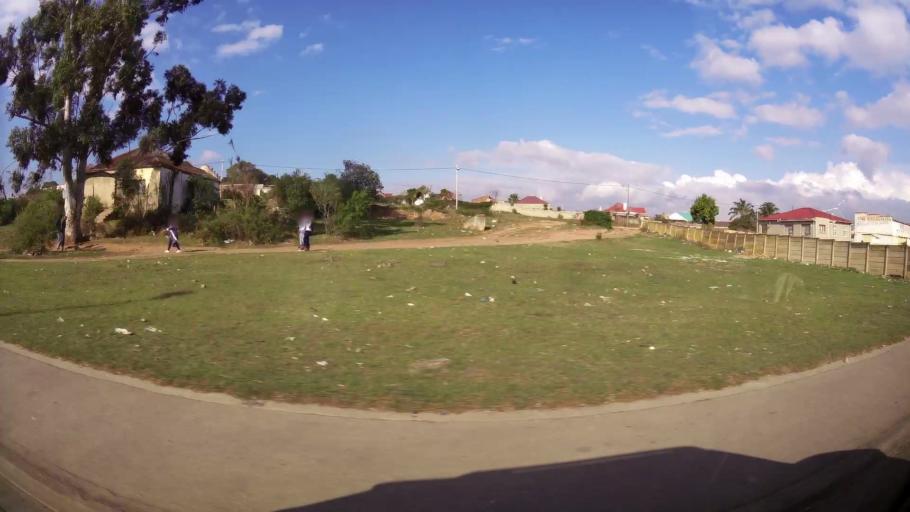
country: ZA
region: Eastern Cape
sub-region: Nelson Mandela Bay Metropolitan Municipality
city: Uitenhage
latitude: -33.7589
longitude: 25.3907
